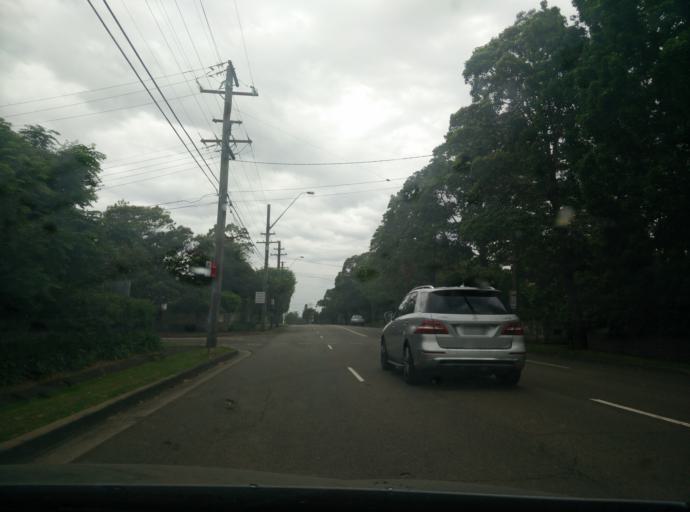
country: AU
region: New South Wales
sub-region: Ku-ring-gai
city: Roseville Chase
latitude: -33.7824
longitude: 151.1881
